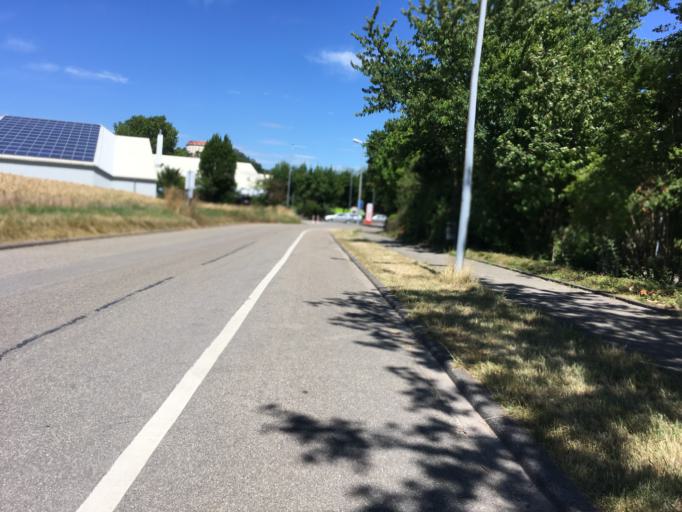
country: DE
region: Baden-Wuerttemberg
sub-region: Regierungsbezirk Stuttgart
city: Vaihingen an der Enz
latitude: 48.9261
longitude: 8.9519
